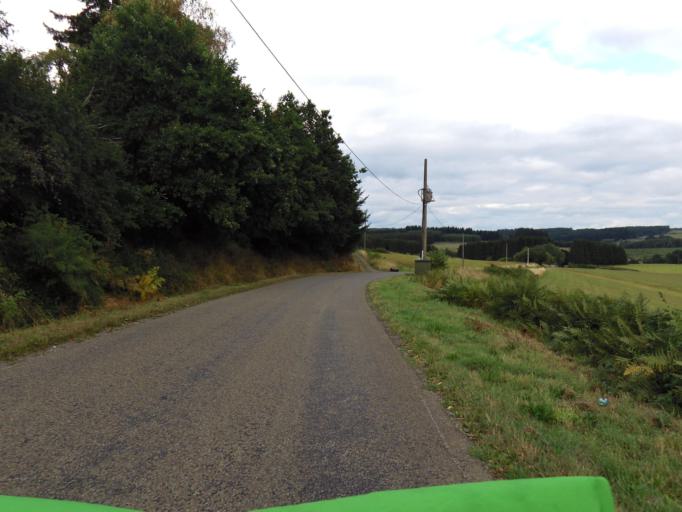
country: BE
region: Wallonia
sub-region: Province de Namur
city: Bievre
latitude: 49.9035
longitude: 4.9952
